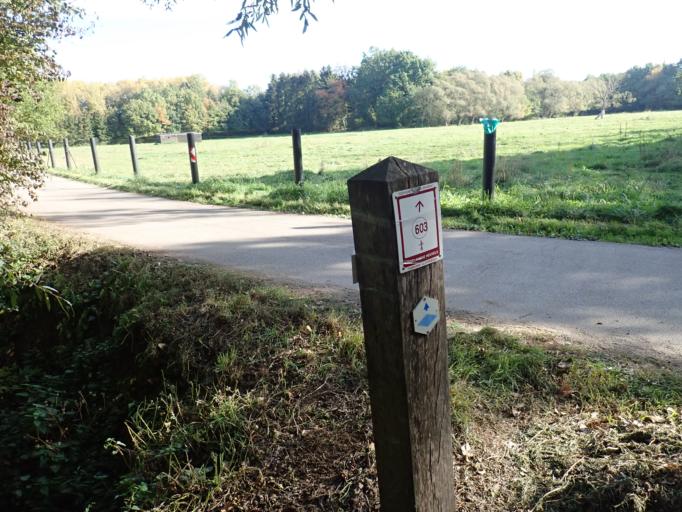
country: BE
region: Flanders
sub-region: Provincie Vlaams-Brabant
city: Holsbeek
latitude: 50.9386
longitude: 4.7633
